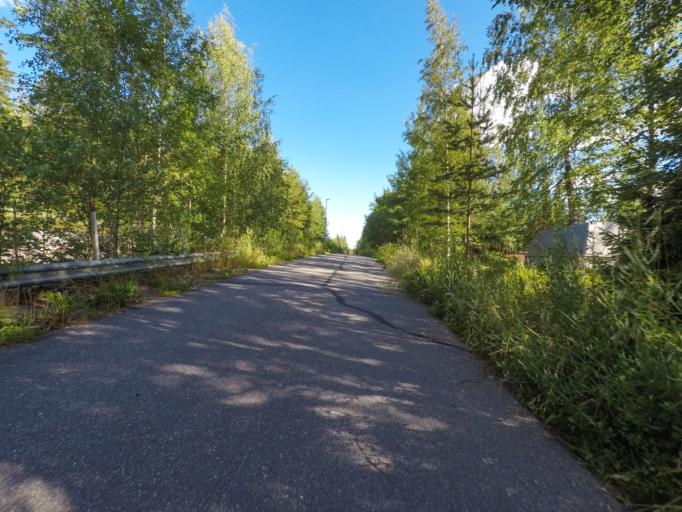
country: FI
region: South Karelia
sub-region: Lappeenranta
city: Lappeenranta
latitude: 61.0917
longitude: 28.1404
